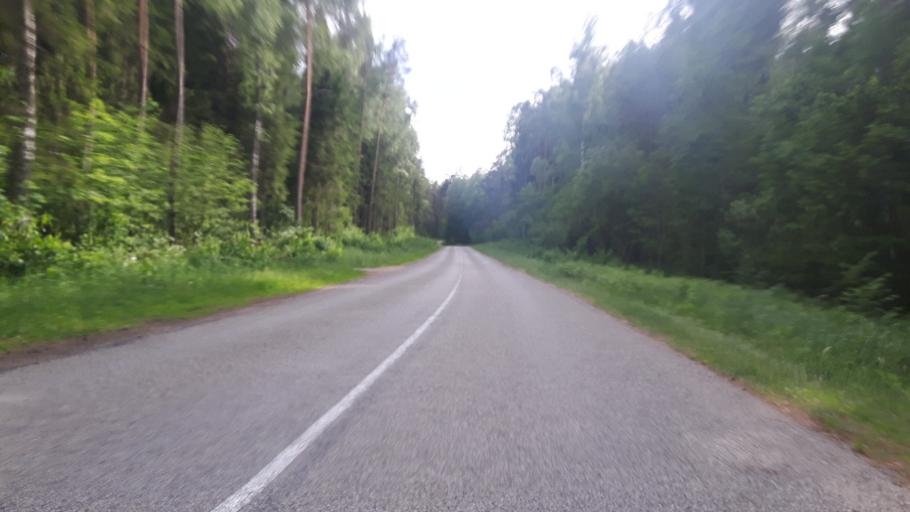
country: LV
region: Engure
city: Smarde
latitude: 56.9946
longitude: 23.3163
